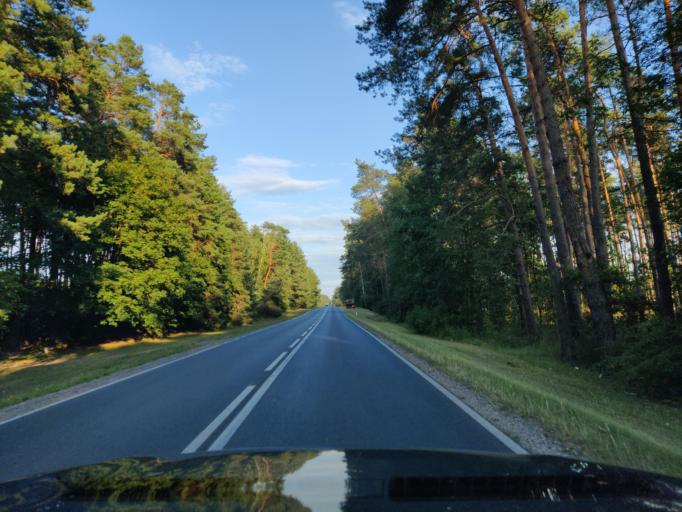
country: PL
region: Masovian Voivodeship
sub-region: Powiat pultuski
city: Pultusk
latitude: 52.6769
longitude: 21.1458
